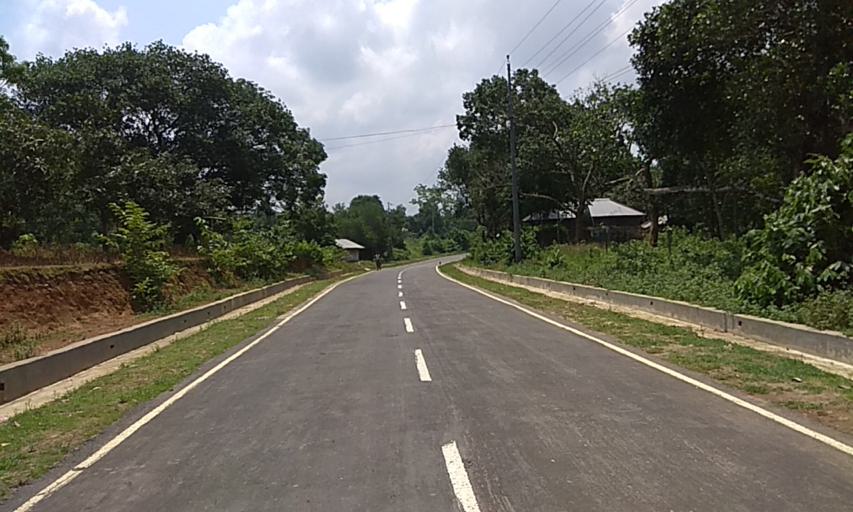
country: BD
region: Chittagong
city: Manikchari
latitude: 22.9375
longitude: 91.8925
